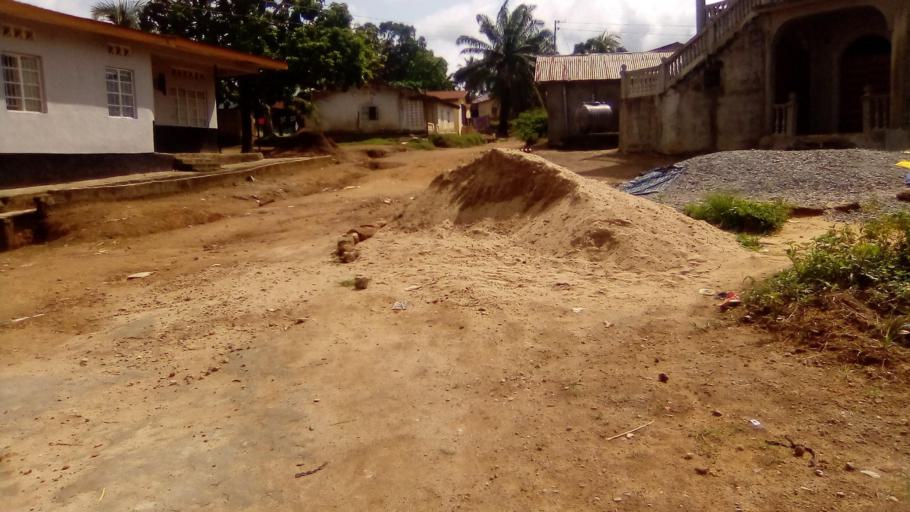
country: SL
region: Southern Province
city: Bo
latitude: 7.9757
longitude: -11.7281
